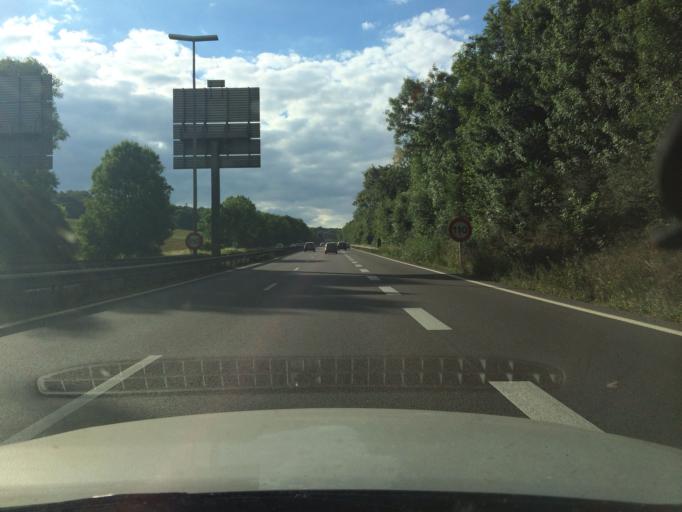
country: FR
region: Lorraine
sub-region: Departement de Meurthe-et-Moselle
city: Ludres
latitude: 48.6295
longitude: 6.1800
